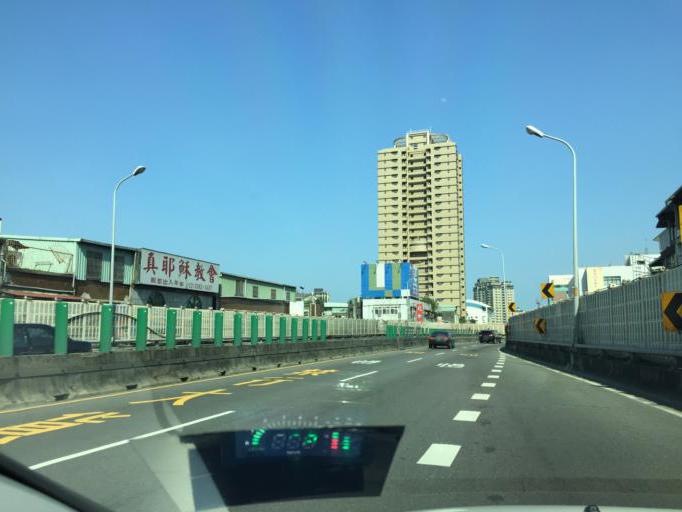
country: TW
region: Taipei
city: Taipei
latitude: 25.0613
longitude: 121.4858
